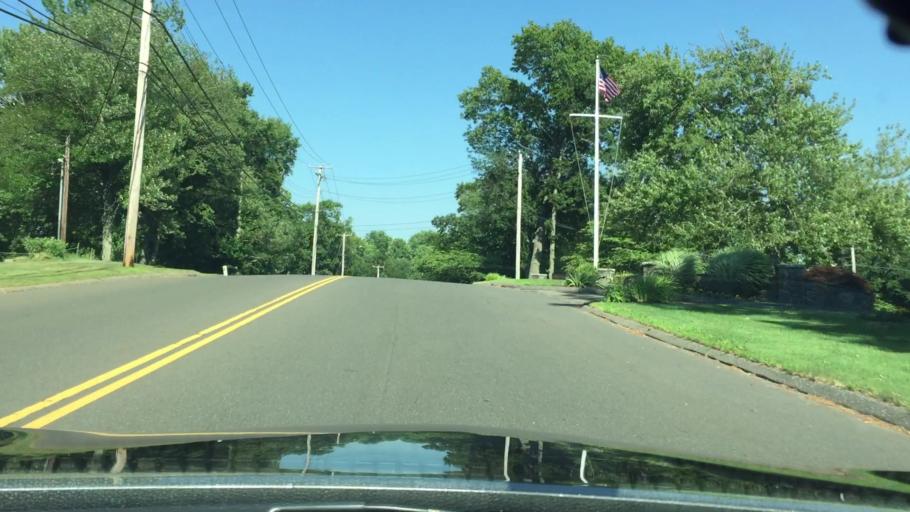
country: US
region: Connecticut
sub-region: New Haven County
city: City of Milford (balance)
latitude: 41.2509
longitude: -73.1143
